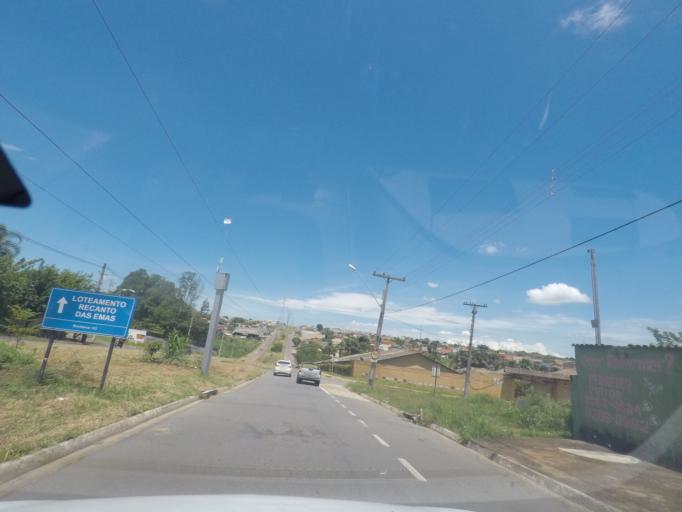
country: BR
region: Goias
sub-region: Goiania
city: Goiania
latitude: -16.7320
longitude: -49.3539
